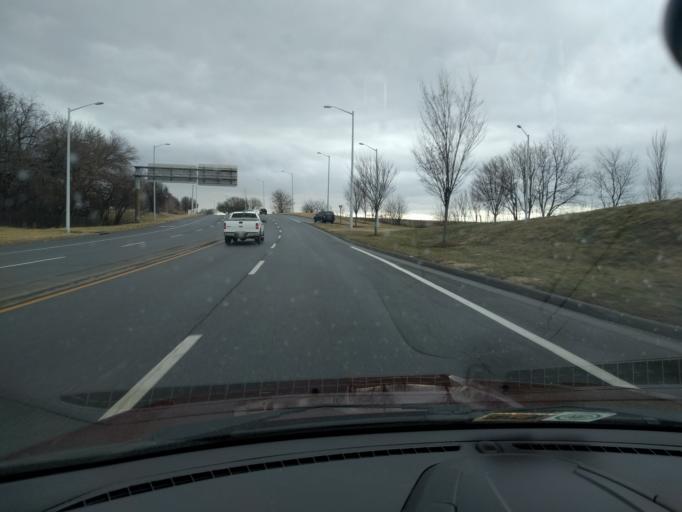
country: US
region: Virginia
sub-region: Roanoke County
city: Hollins
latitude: 37.3121
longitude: -79.9659
